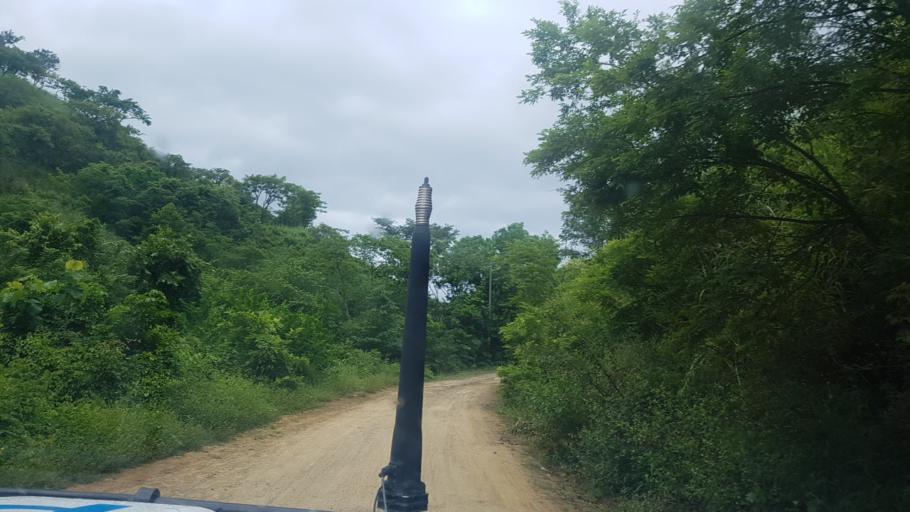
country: HN
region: El Paraiso
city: Oropoli
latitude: 13.7393
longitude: -86.7012
